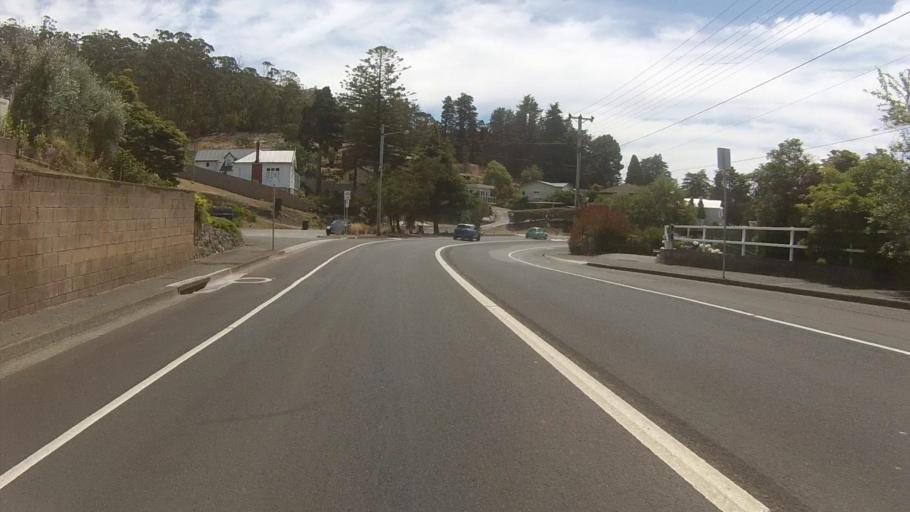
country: AU
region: Tasmania
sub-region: Kingborough
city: Taroona
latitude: -42.9289
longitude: 147.3597
